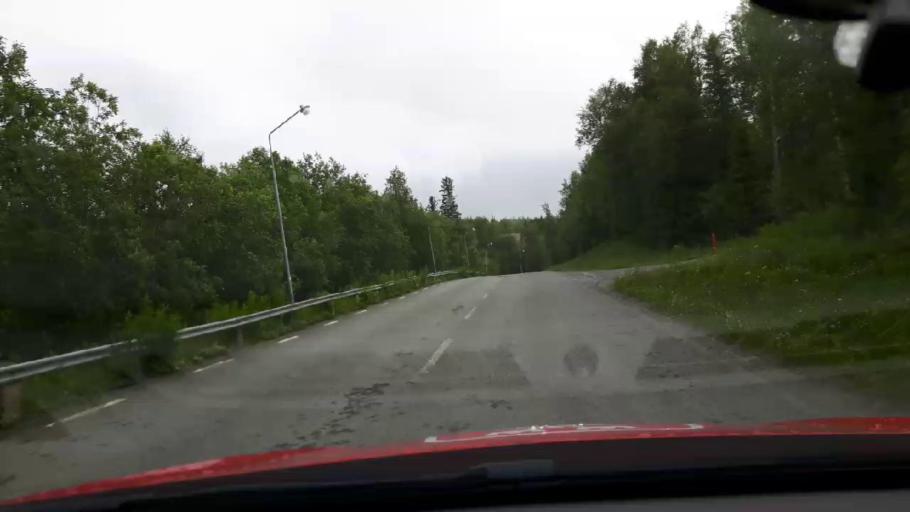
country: SE
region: Jaemtland
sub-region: Are Kommun
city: Are
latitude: 63.2538
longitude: 12.4535
